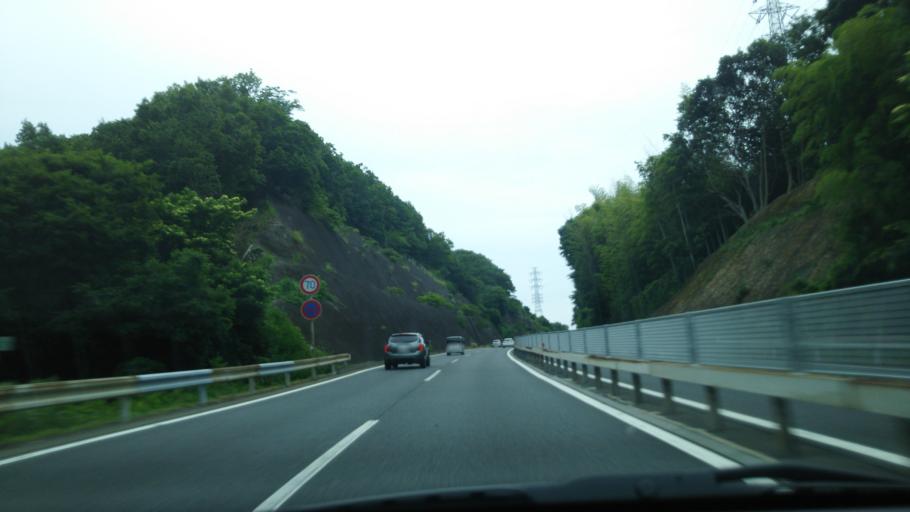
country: JP
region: Kanagawa
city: Oiso
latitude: 35.3249
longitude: 139.2818
